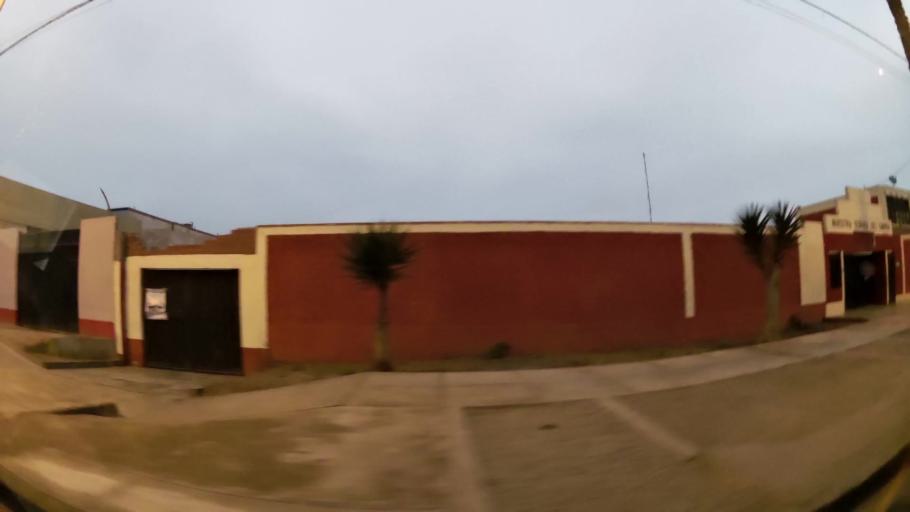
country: PE
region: Callao
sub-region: Callao
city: Callao
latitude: -12.0810
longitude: -77.1004
